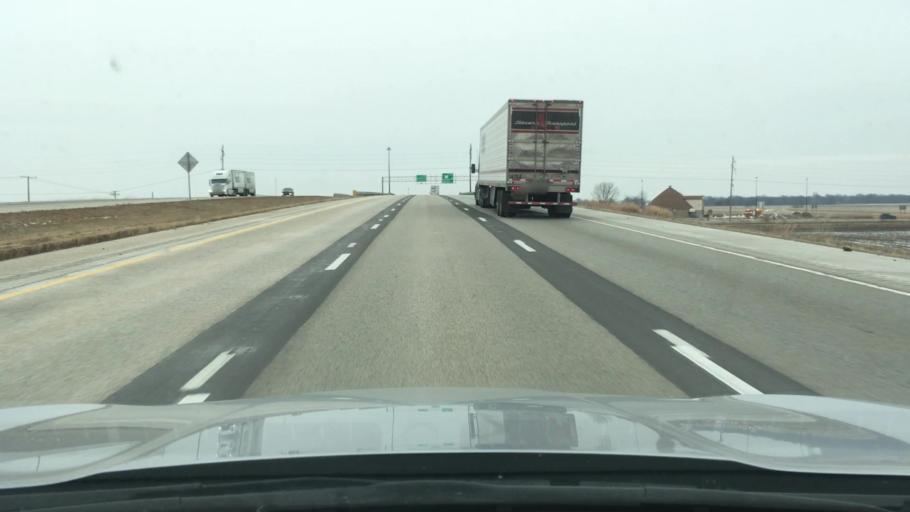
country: US
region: Illinois
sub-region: Sangamon County
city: Divernon
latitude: 39.5883
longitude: -89.6466
